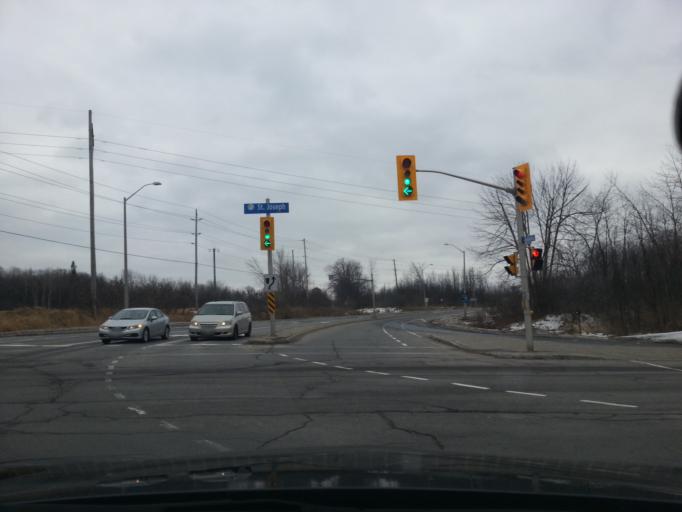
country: CA
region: Quebec
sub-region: Outaouais
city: Gatineau
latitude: 45.4533
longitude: -75.5753
